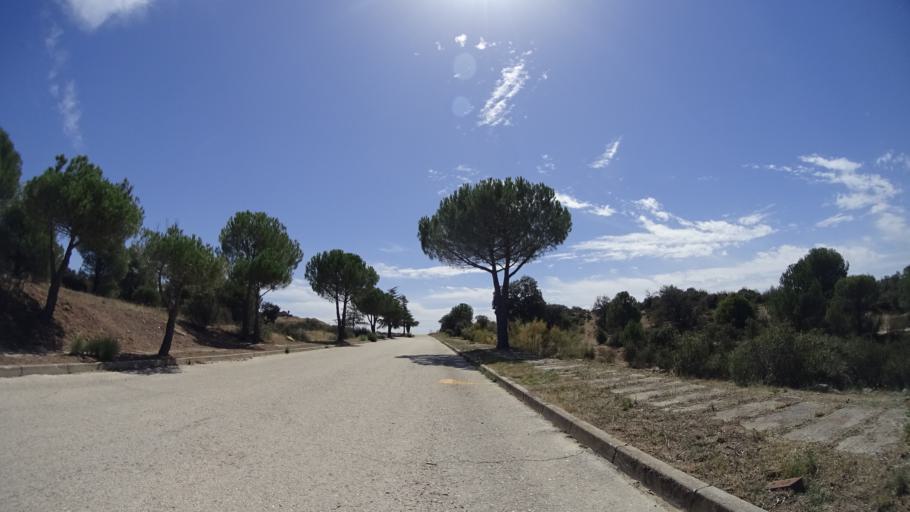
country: ES
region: Madrid
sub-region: Provincia de Madrid
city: Torrelodones
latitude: 40.5702
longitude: -3.9400
